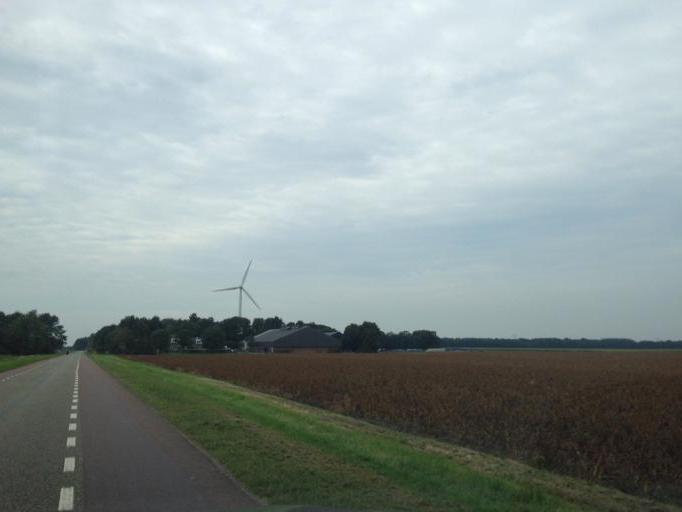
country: NL
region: Flevoland
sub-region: Gemeente Lelystad
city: Lelystad
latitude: 52.4126
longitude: 5.4129
